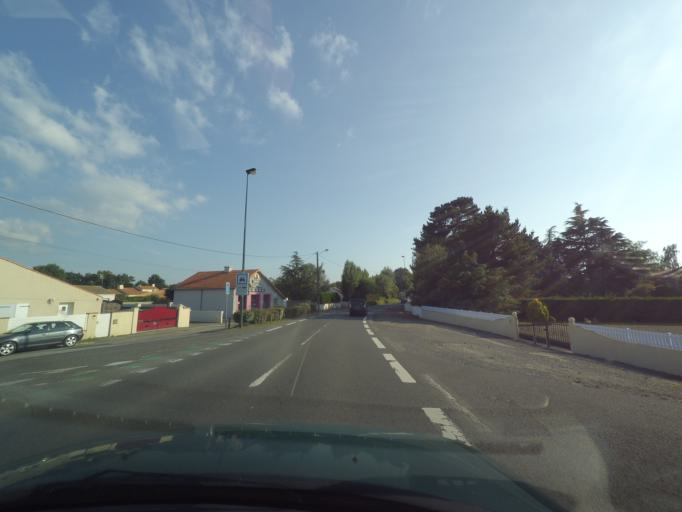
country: FR
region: Pays de la Loire
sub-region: Departement de la Loire-Atlantique
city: Saint-Philbert-de-Grand-Lieu
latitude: 47.0463
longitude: -1.6385
